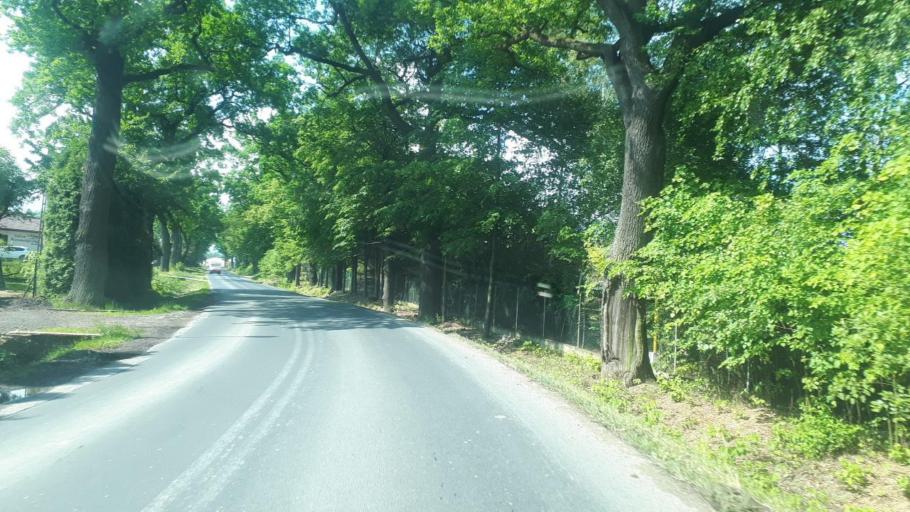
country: PL
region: Silesian Voivodeship
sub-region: Powiat bielski
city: Wilamowice
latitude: 49.9361
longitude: 19.1254
